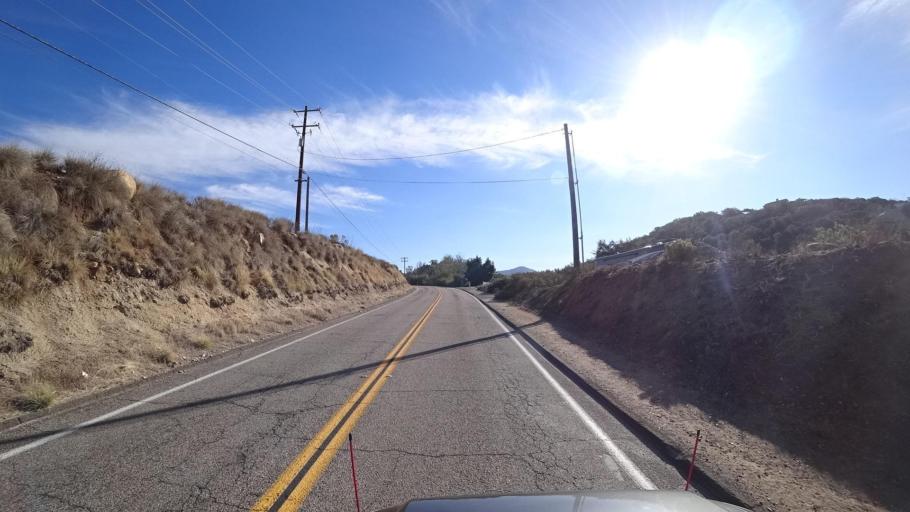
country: US
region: California
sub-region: San Diego County
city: Alpine
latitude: 32.8158
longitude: -116.7665
